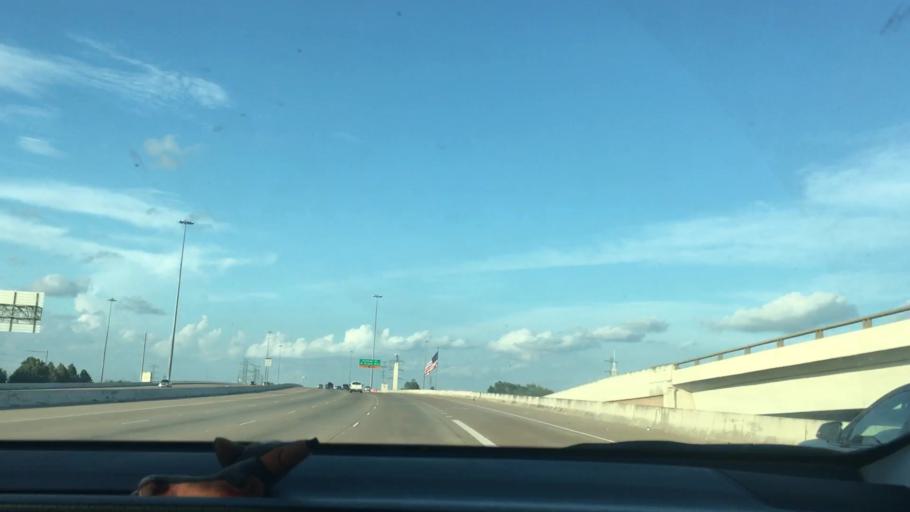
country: US
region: Texas
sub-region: Fort Bend County
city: Meadows Place
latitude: 29.6243
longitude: -95.5972
